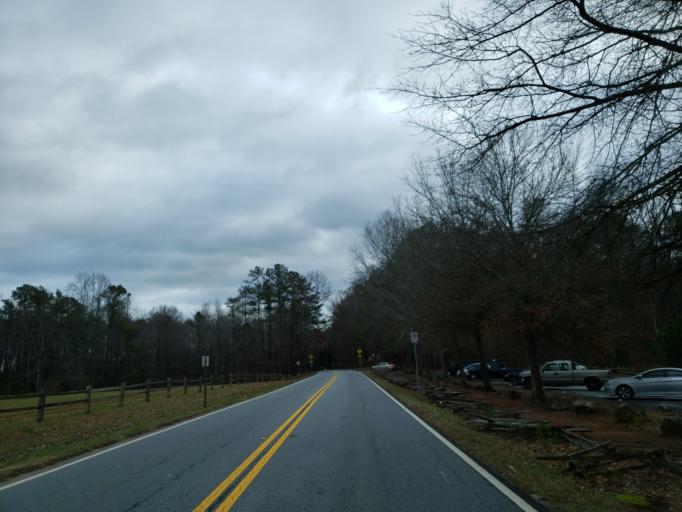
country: US
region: Georgia
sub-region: Cobb County
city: Marietta
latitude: 33.9332
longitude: -84.6046
